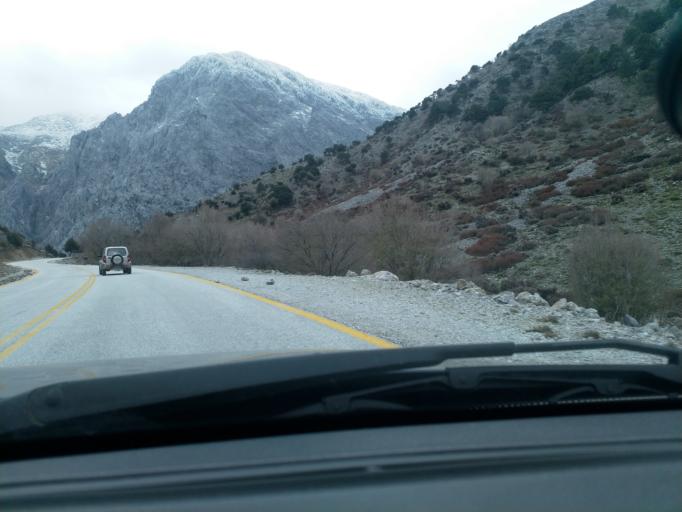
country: GR
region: Crete
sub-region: Nomos Chanias
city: Perivolia
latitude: 35.3116
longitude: 23.9165
